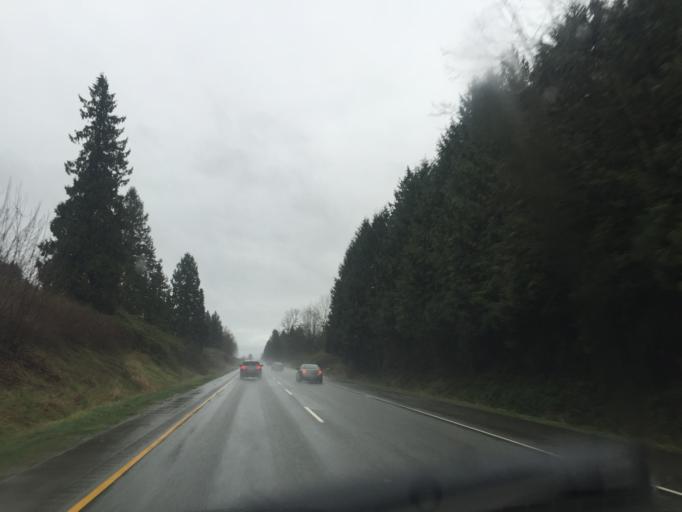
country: CA
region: British Columbia
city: Aldergrove
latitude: 49.0743
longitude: -122.4239
